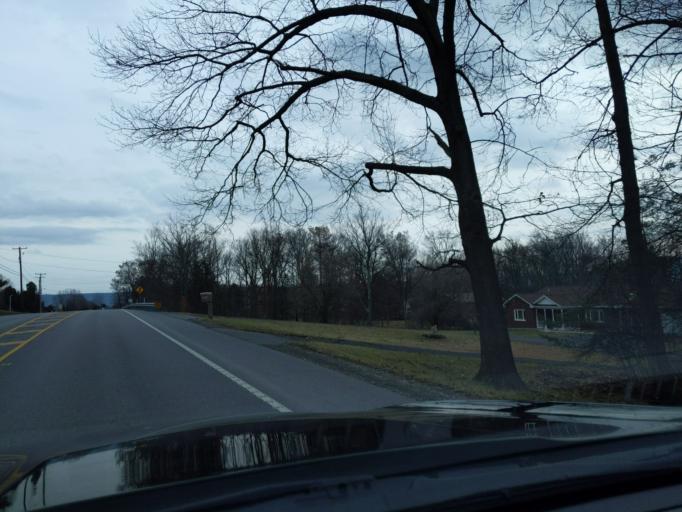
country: US
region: Pennsylvania
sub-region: Blair County
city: Lakemont
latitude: 40.4631
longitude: -78.3791
